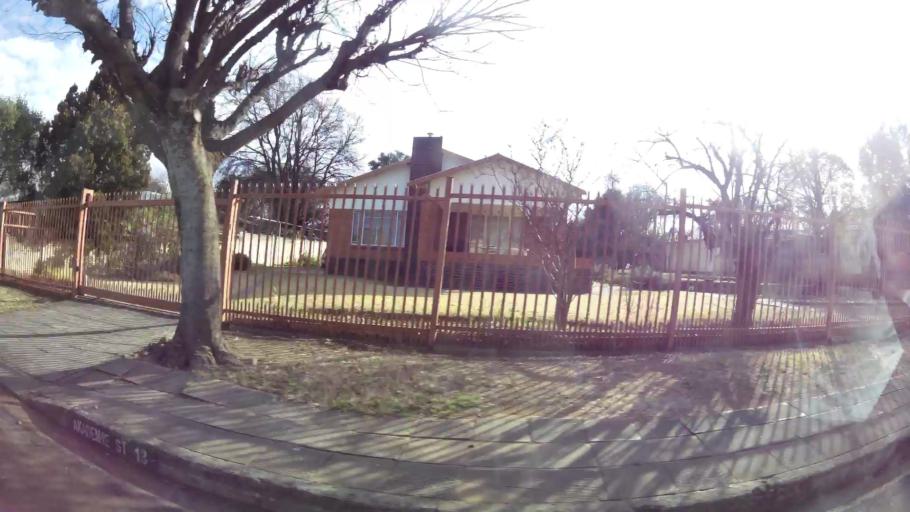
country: ZA
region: Orange Free State
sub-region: Mangaung Metropolitan Municipality
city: Bloemfontein
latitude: -29.0790
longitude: 26.2141
